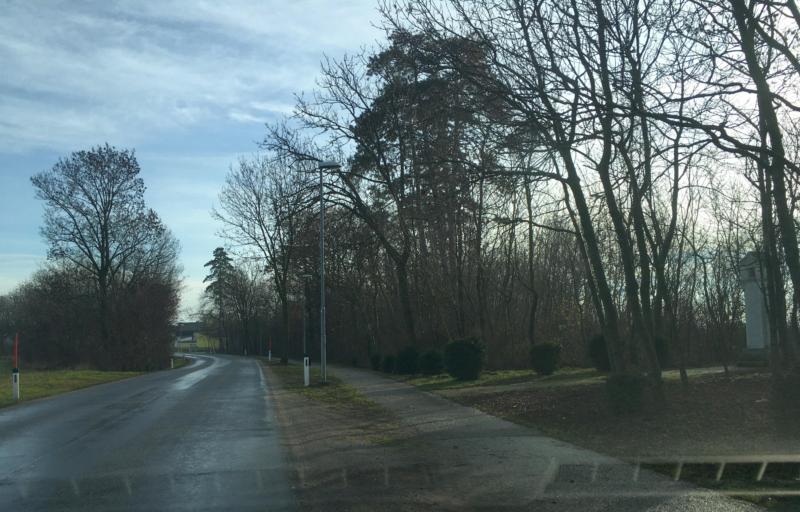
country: AT
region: Lower Austria
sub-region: Politischer Bezirk Ganserndorf
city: Orth an der Donau
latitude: 48.1833
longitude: 16.7348
